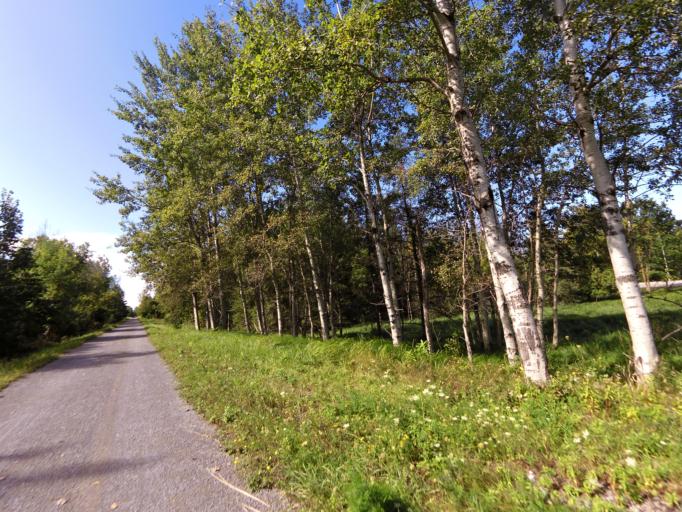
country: CA
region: Ontario
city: Bells Corners
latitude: 45.3156
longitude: -75.8470
